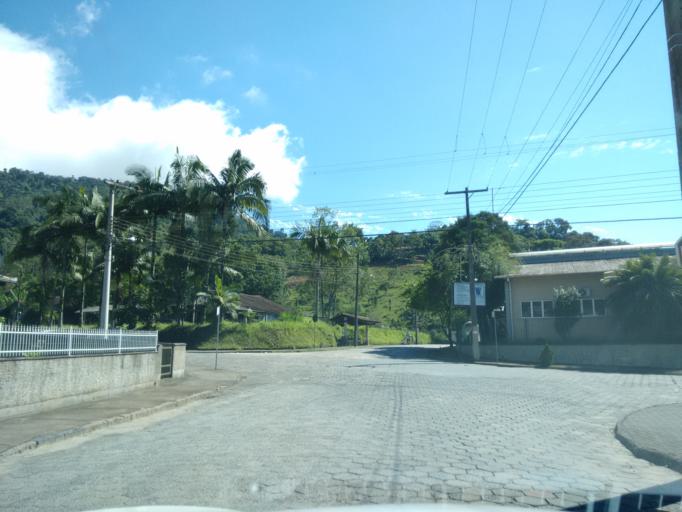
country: BR
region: Santa Catarina
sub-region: Pomerode
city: Pomerode
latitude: -26.7518
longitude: -49.1819
